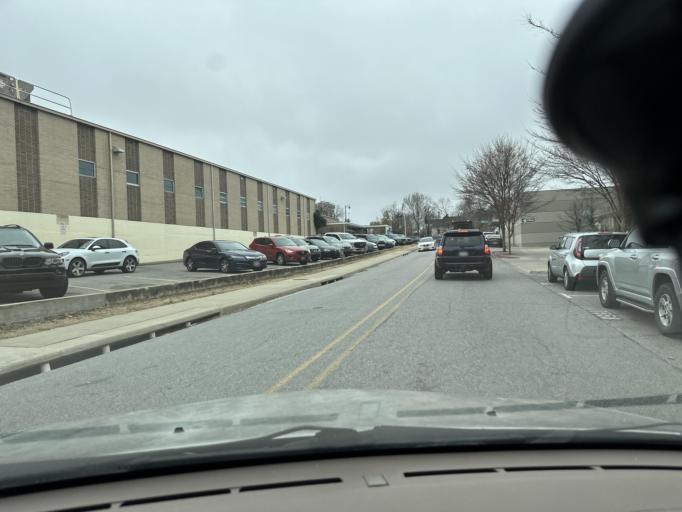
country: US
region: Arkansas
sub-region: Washington County
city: Fayetteville
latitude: 36.0674
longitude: -94.1608
